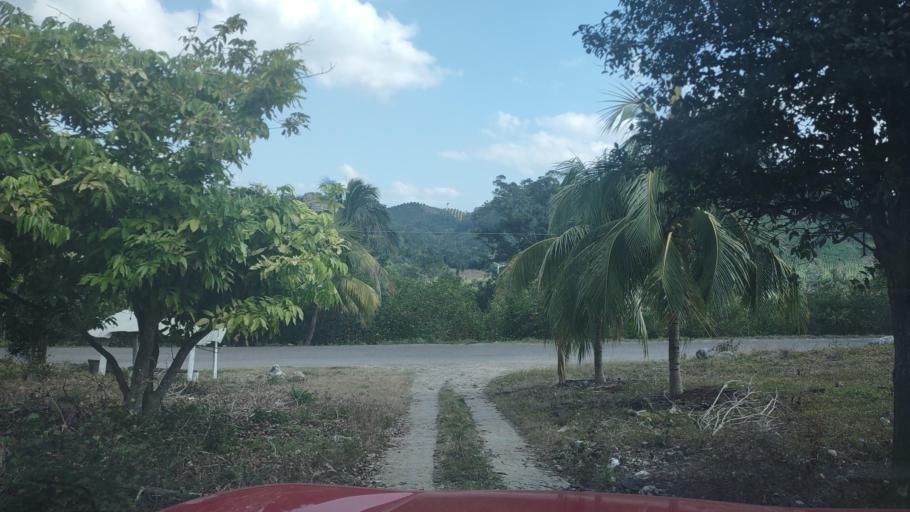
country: MX
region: Veracruz
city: Agua Dulce
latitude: 20.3051
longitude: -97.1736
